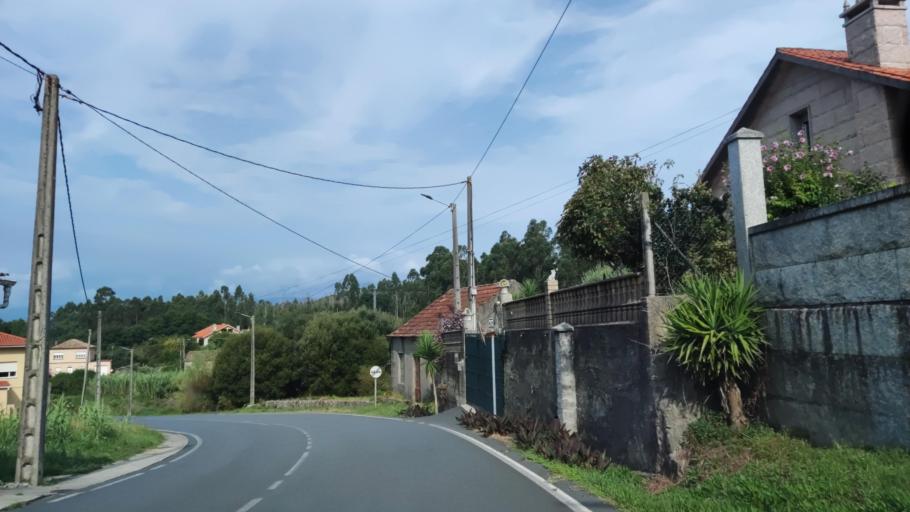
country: ES
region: Galicia
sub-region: Provincia da Coruna
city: Rianxo
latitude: 42.6479
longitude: -8.7945
